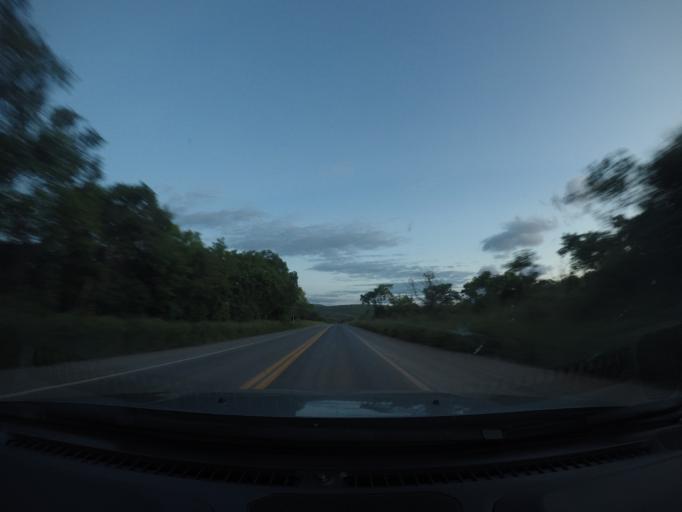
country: BR
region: Bahia
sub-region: Seabra
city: Seabra
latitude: -12.4847
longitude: -41.7364
